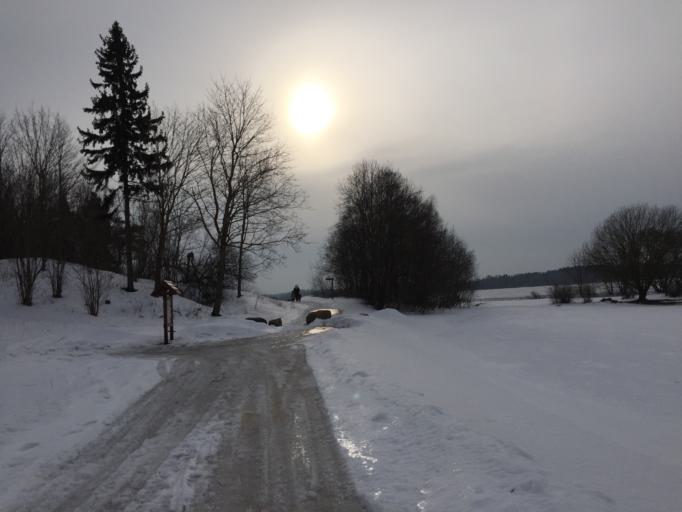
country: LV
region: Ikskile
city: Ikskile
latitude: 56.8446
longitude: 24.4528
